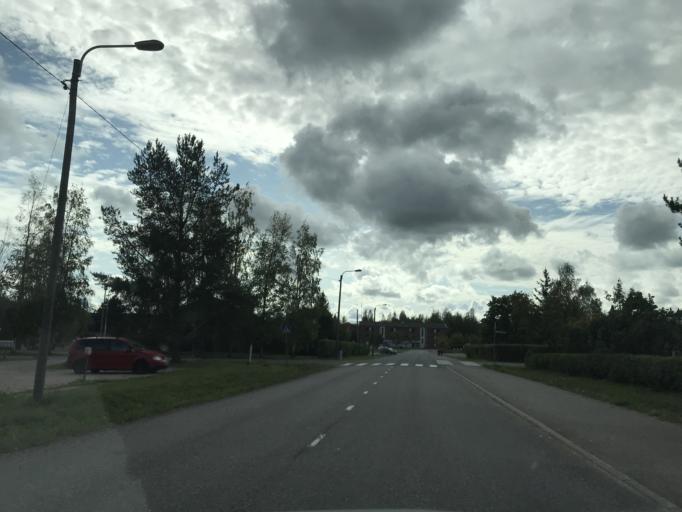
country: FI
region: Paijanne Tavastia
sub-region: Lahti
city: Orimattila
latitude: 60.8117
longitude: 25.7256
